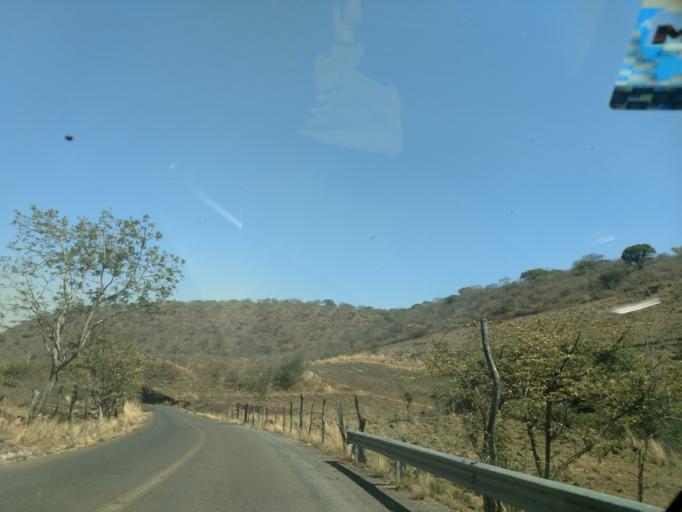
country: MX
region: Nayarit
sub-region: Tepic
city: La Corregidora
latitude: 21.4775
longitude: -104.6734
